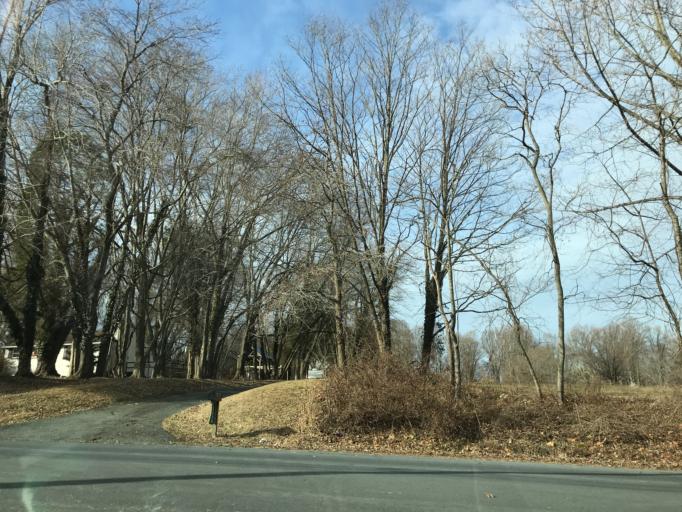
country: US
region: Maryland
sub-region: Harford County
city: Joppatowne
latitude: 39.4485
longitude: -76.3733
